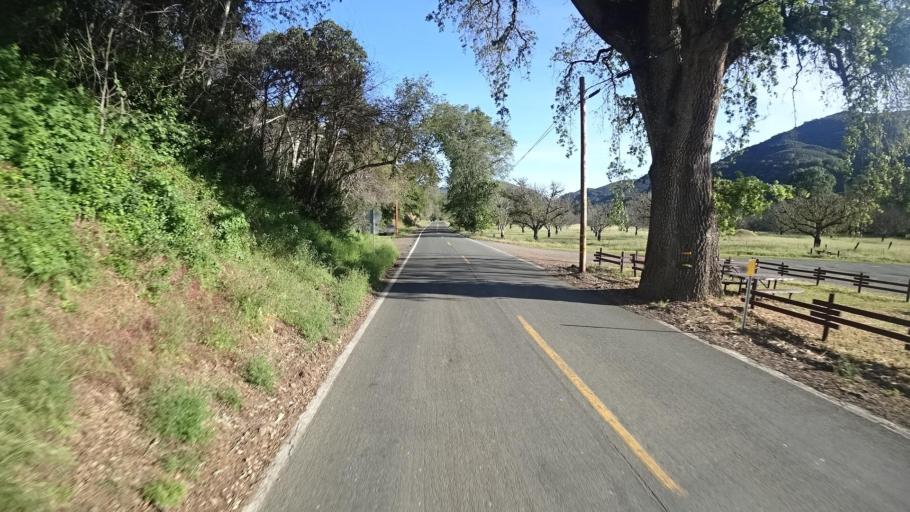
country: US
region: California
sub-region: Lake County
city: Upper Lake
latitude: 39.1267
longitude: -122.9955
